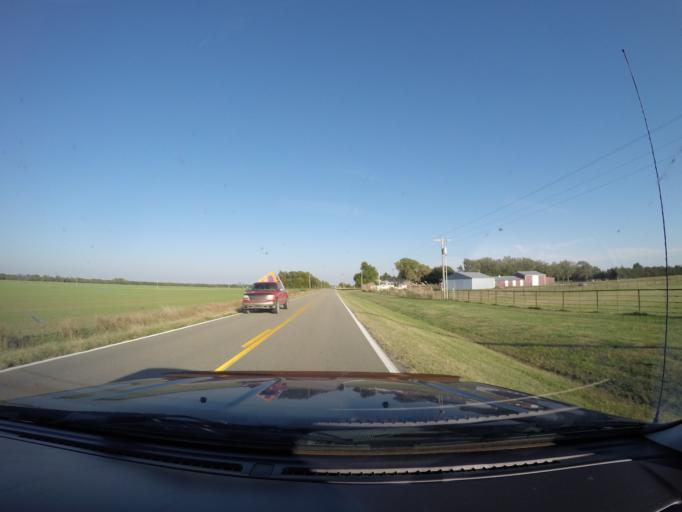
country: US
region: Kansas
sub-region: Saline County
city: Salina
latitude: 38.8418
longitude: -97.7454
